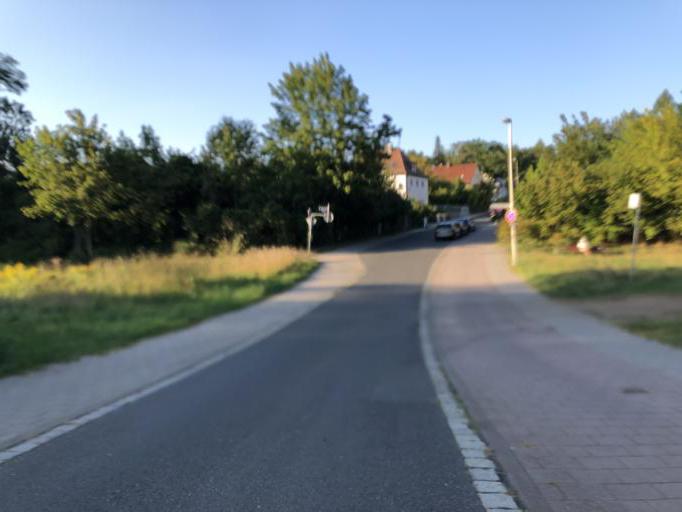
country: DE
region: Bavaria
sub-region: Regierungsbezirk Mittelfranken
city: Erlangen
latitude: 49.5992
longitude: 11.0263
